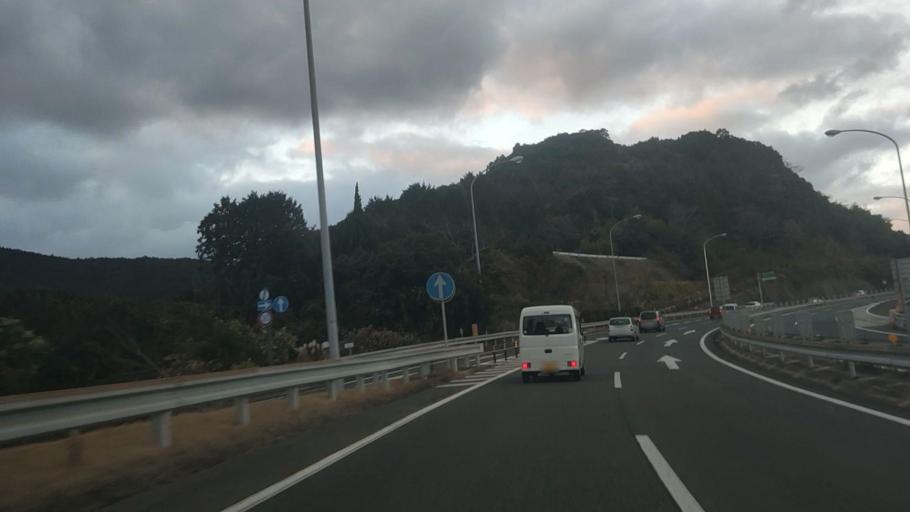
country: JP
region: Nagasaki
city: Obita
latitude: 32.8127
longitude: 129.9572
